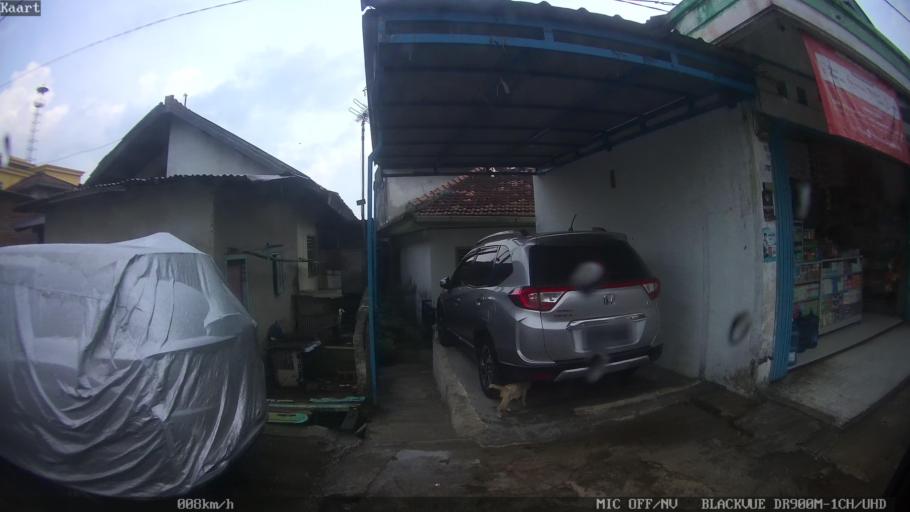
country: ID
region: Lampung
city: Bandarlampung
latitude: -5.4388
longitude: 105.2761
